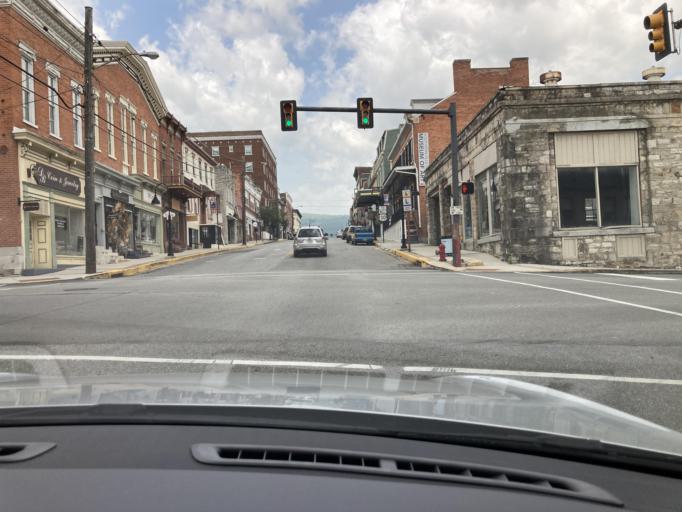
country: US
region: Pennsylvania
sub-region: Bedford County
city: Bedford
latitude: 40.0192
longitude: -78.5016
